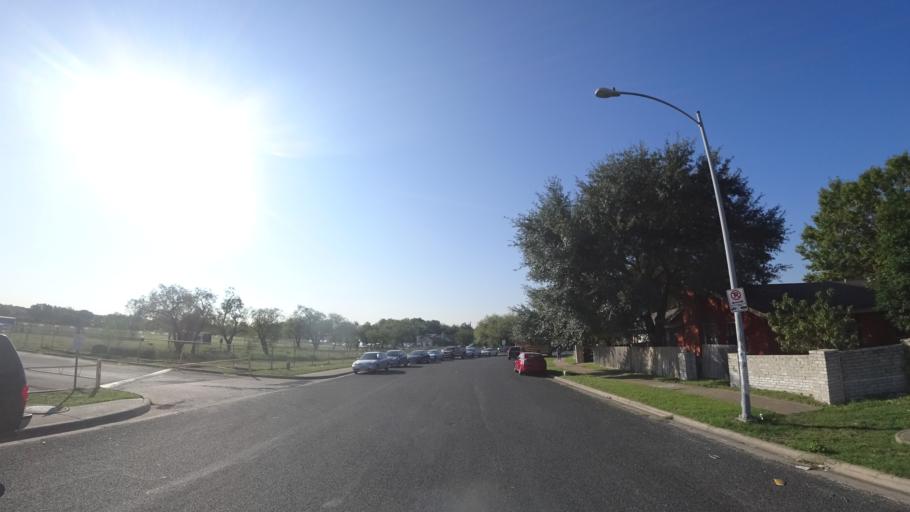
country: US
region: Texas
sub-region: Travis County
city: Austin
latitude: 30.3116
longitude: -97.6578
